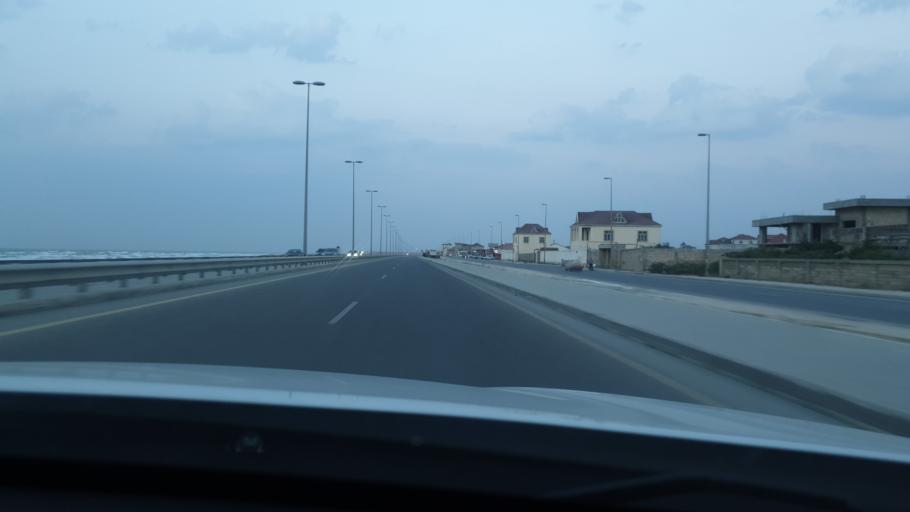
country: AZ
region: Baki
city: Bilajer
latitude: 40.5866
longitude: 50.0355
